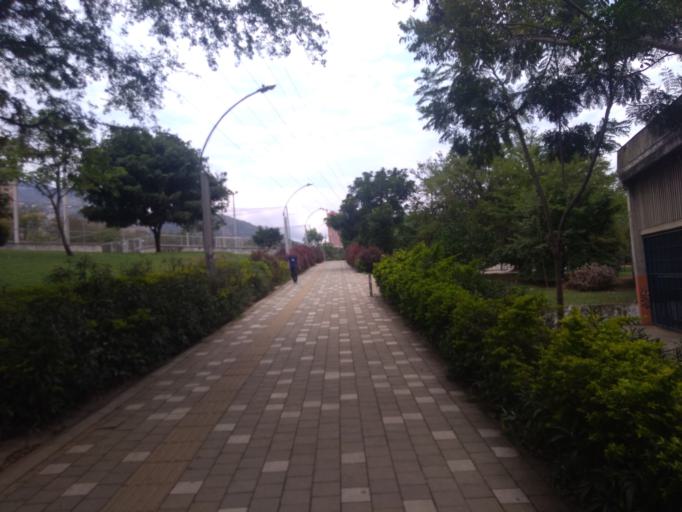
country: CO
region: Antioquia
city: Bello
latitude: 6.3357
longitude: -75.5467
